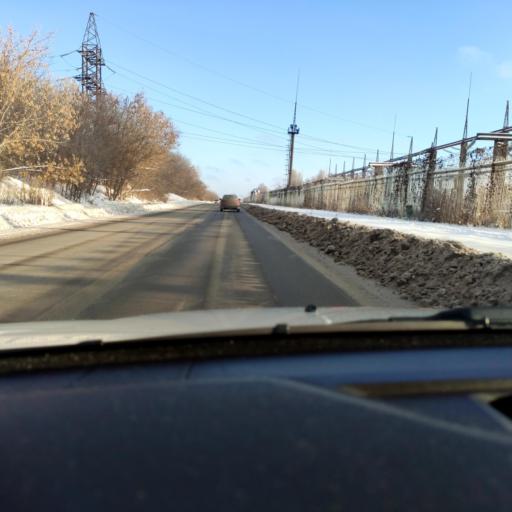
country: RU
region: Samara
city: Petra-Dubrava
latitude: 53.2529
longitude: 50.2738
